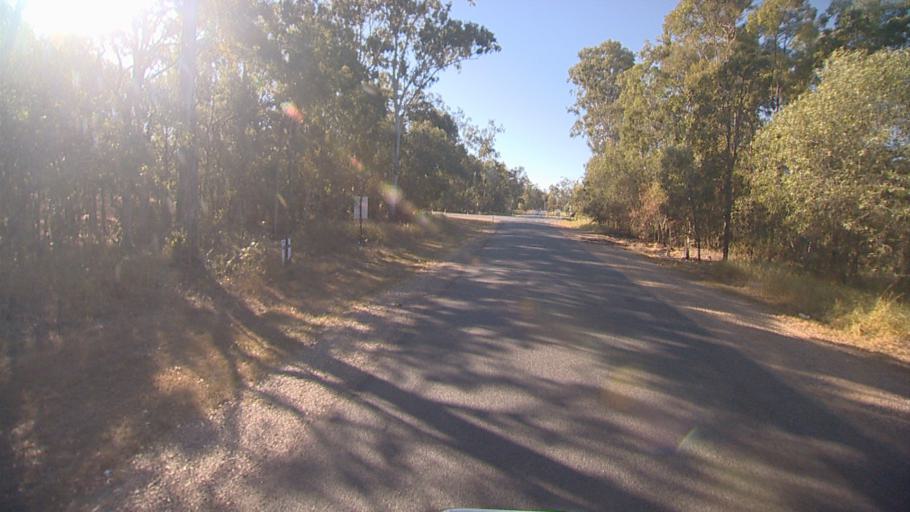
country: AU
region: Queensland
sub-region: Logan
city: North Maclean
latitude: -27.7936
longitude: 153.0267
